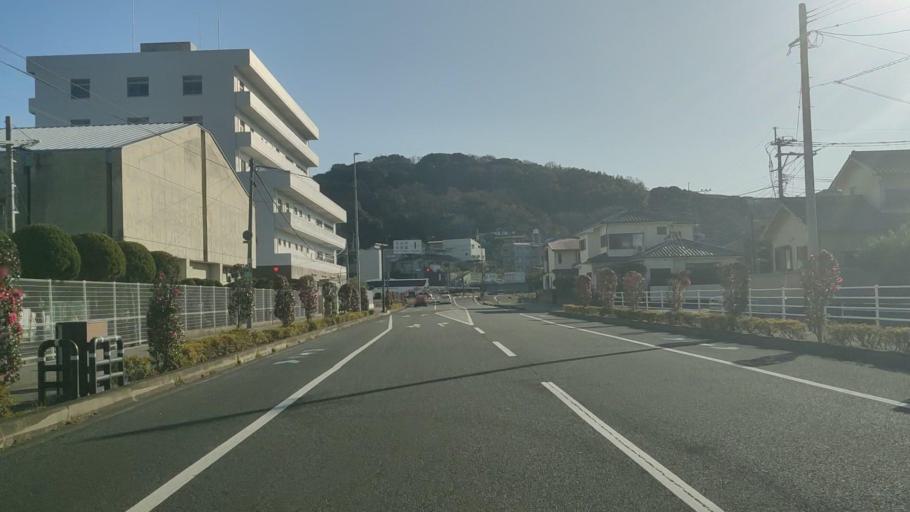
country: JP
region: Oita
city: Oita
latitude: 33.2289
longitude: 131.6013
